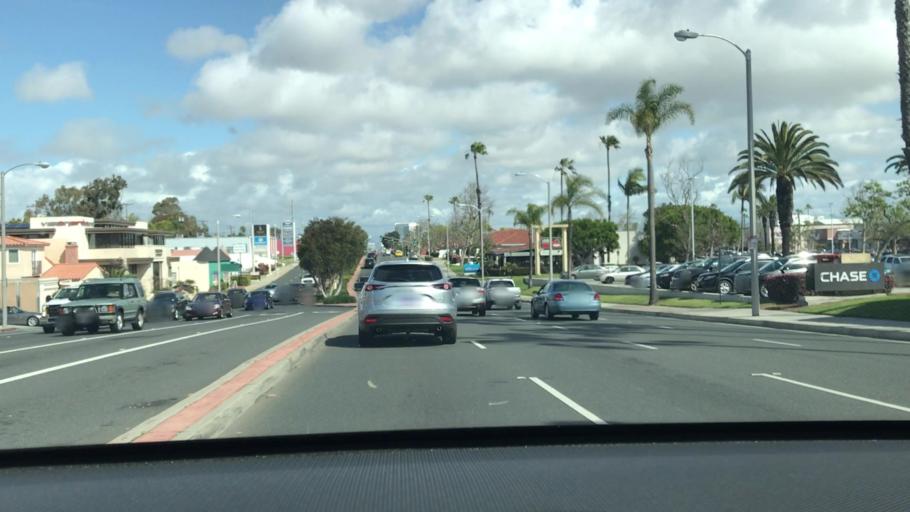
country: US
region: California
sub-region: Los Angeles County
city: Manhattan Beach
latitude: 33.8949
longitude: -118.3960
